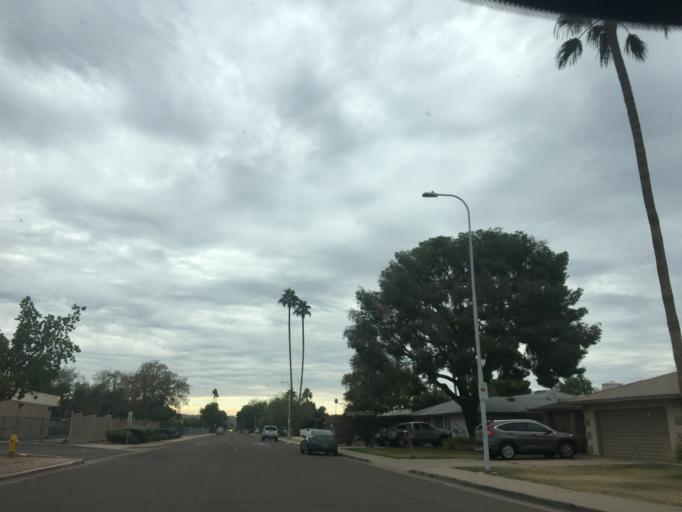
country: US
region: Arizona
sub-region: Maricopa County
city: Guadalupe
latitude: 33.3674
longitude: -111.9213
